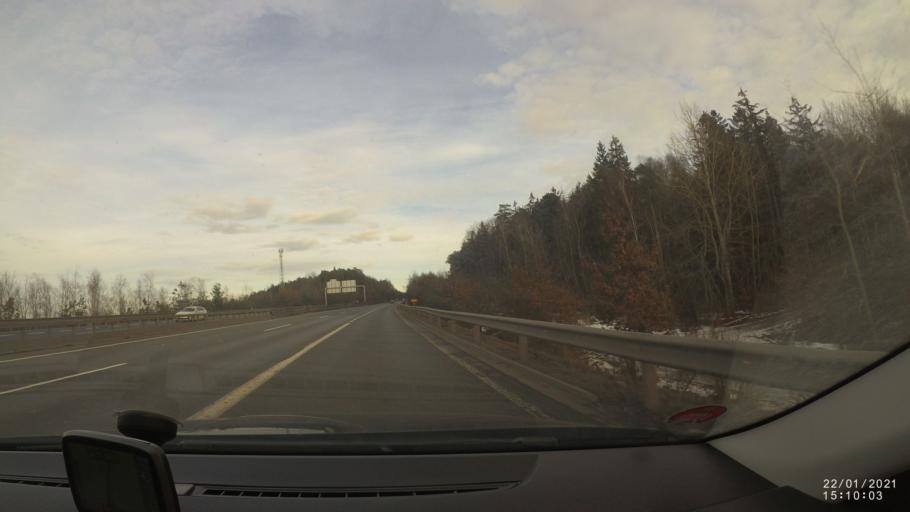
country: CZ
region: Plzensky
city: Dysina
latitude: 49.7373
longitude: 13.5167
